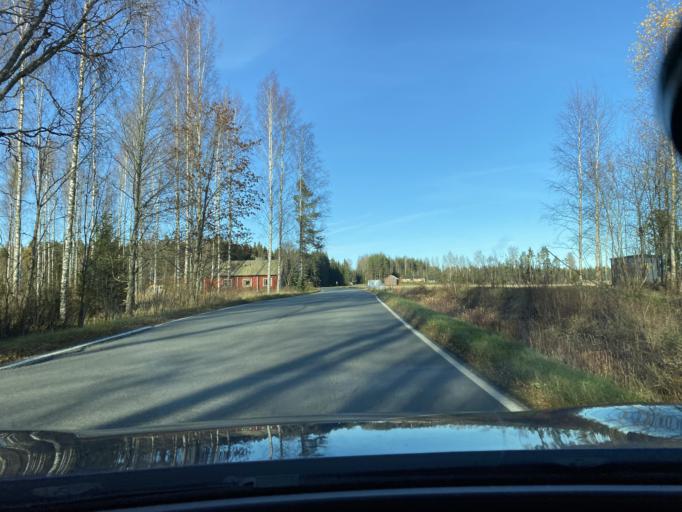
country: FI
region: Haeme
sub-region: Forssa
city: Tammela
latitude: 60.8835
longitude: 23.8445
